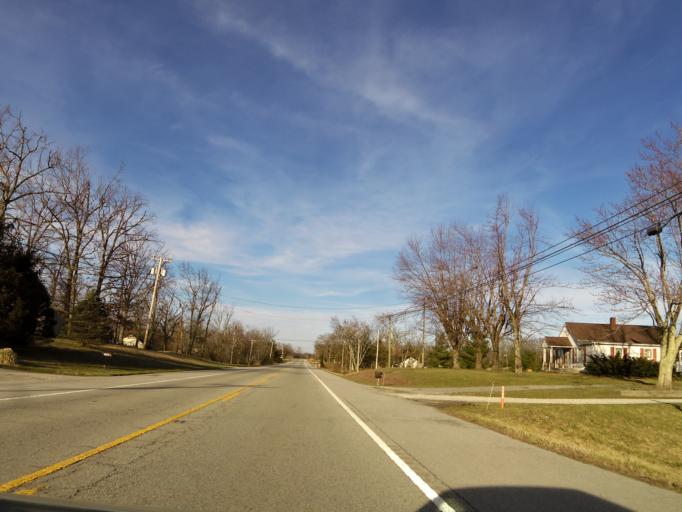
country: US
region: Tennessee
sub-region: White County
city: Sparta
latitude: 35.9358
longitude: -85.3738
